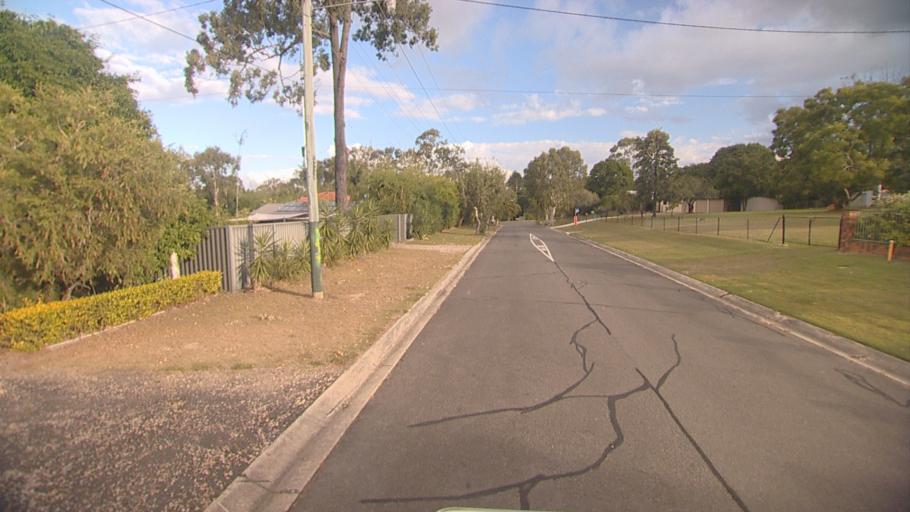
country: AU
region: Queensland
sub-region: Logan
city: Park Ridge South
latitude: -27.7081
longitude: 153.0198
